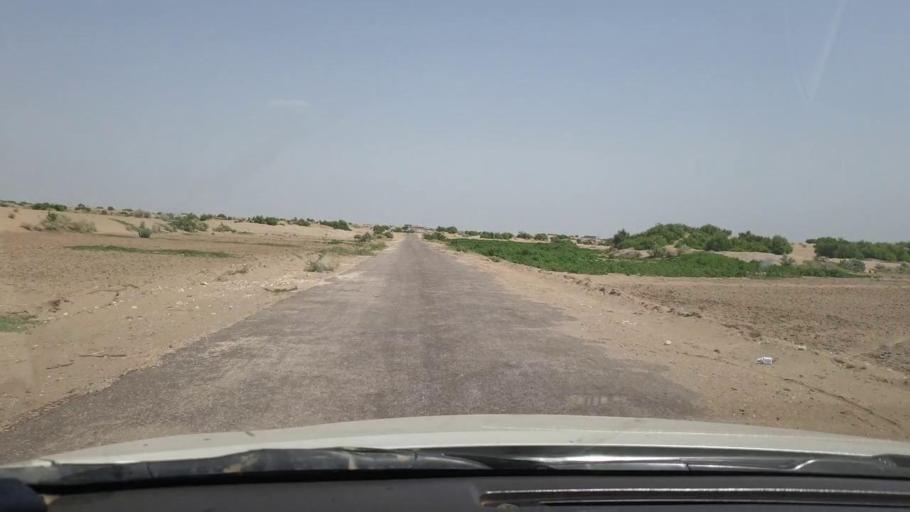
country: PK
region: Sindh
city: Rohri
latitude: 27.4944
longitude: 69.0463
